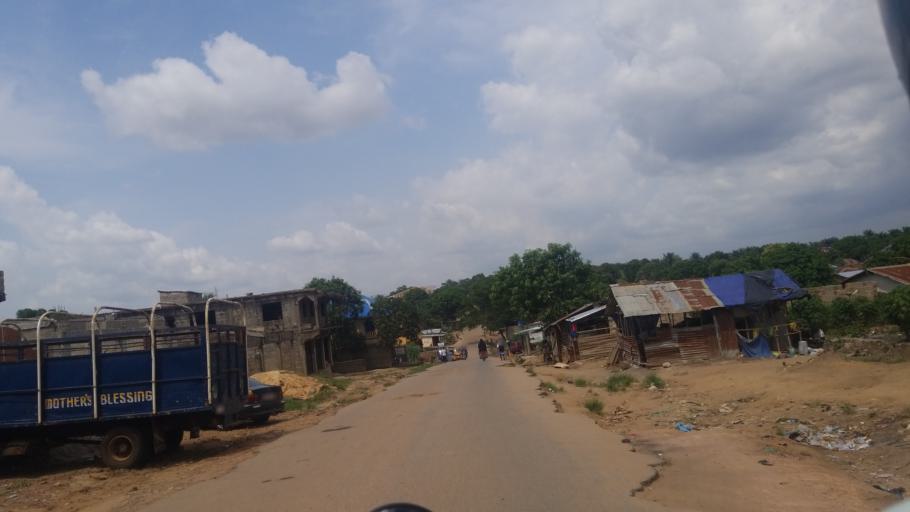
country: SL
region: Western Area
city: Waterloo
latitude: 8.3303
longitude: -13.0483
